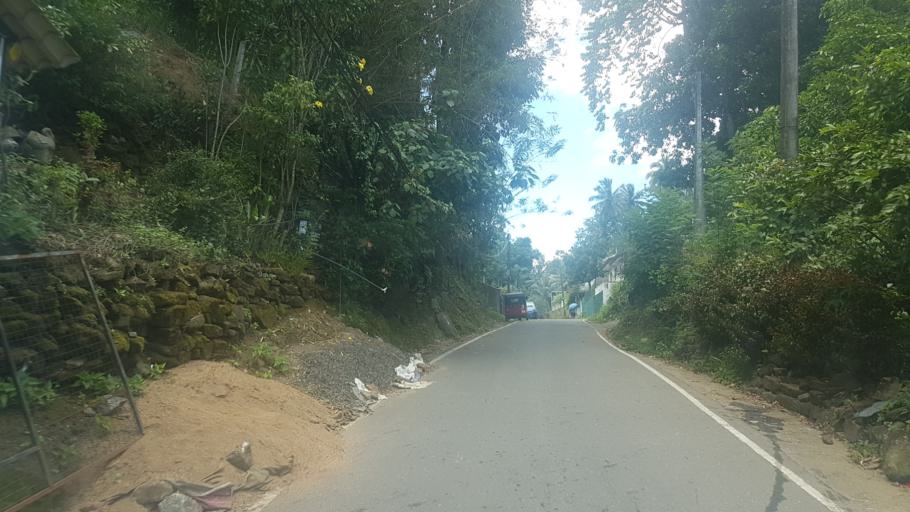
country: LK
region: Central
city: Gampola
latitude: 7.2145
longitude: 80.5924
